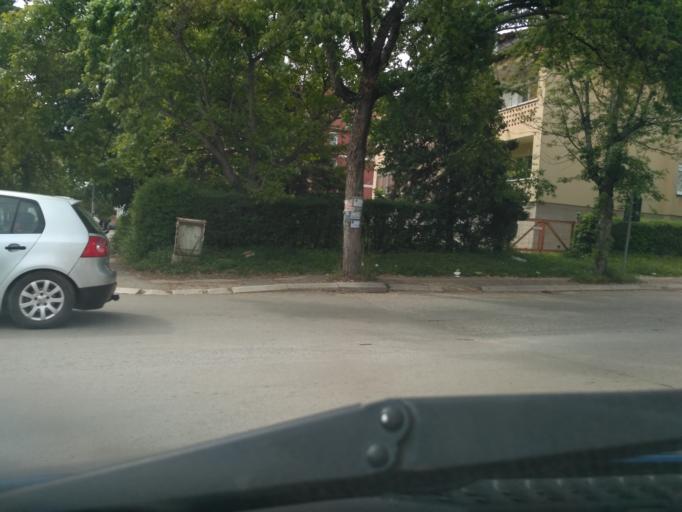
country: RS
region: Central Serbia
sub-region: Podunavski Okrug
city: Smederevska Palanka
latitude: 44.3641
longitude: 20.9671
